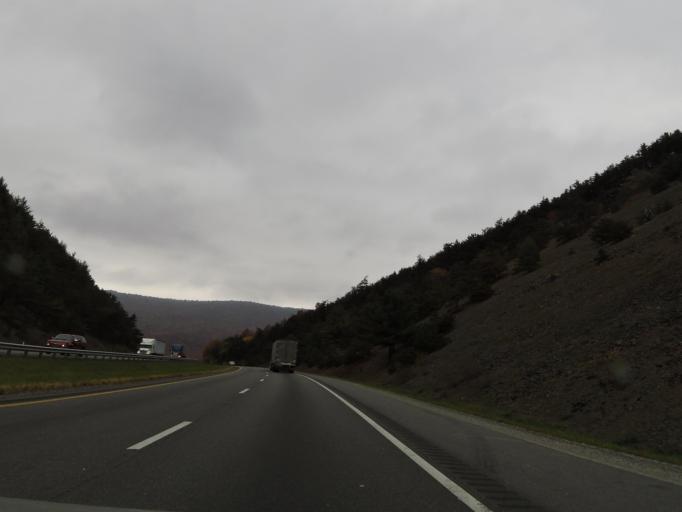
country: US
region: Virginia
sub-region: Bland County
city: Bland
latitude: 37.0252
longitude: -81.1069
